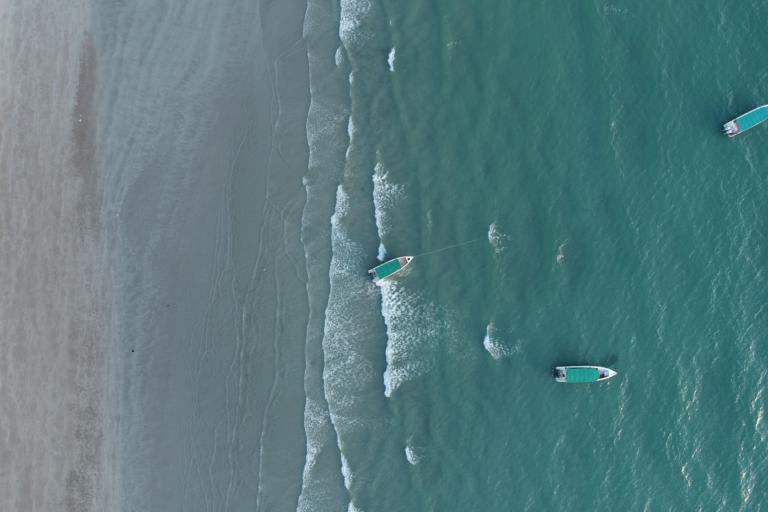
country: TH
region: Rayong
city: Rayong
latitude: 12.5921
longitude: 101.4138
